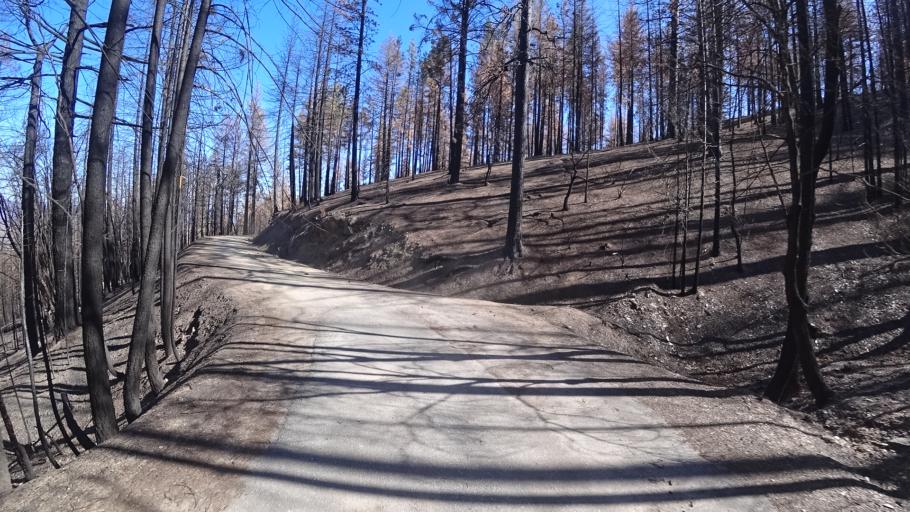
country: US
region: California
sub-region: Tehama County
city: Rancho Tehama Reserve
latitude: 39.6630
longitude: -122.7126
